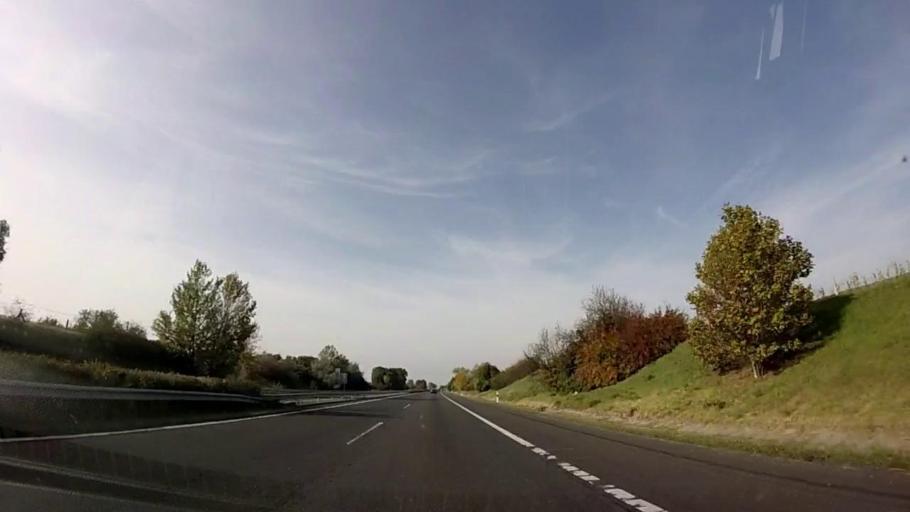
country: HU
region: Somogy
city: Siofok
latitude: 46.8909
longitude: 18.0434
